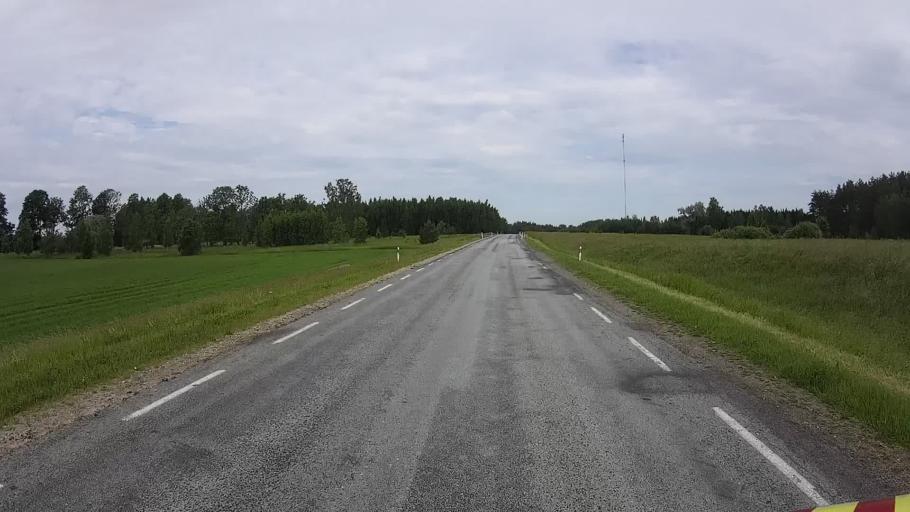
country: EE
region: Viljandimaa
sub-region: Viljandi linn
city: Viljandi
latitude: 58.2314
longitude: 25.6017
